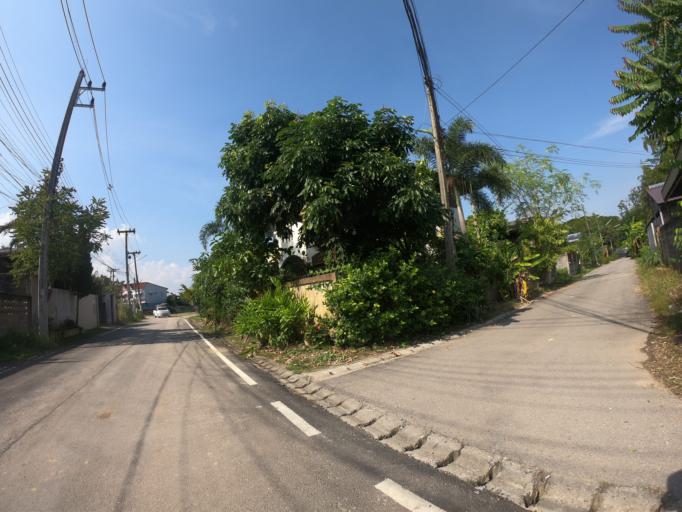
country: TH
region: Chiang Mai
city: Chiang Mai
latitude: 18.8220
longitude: 99.0064
